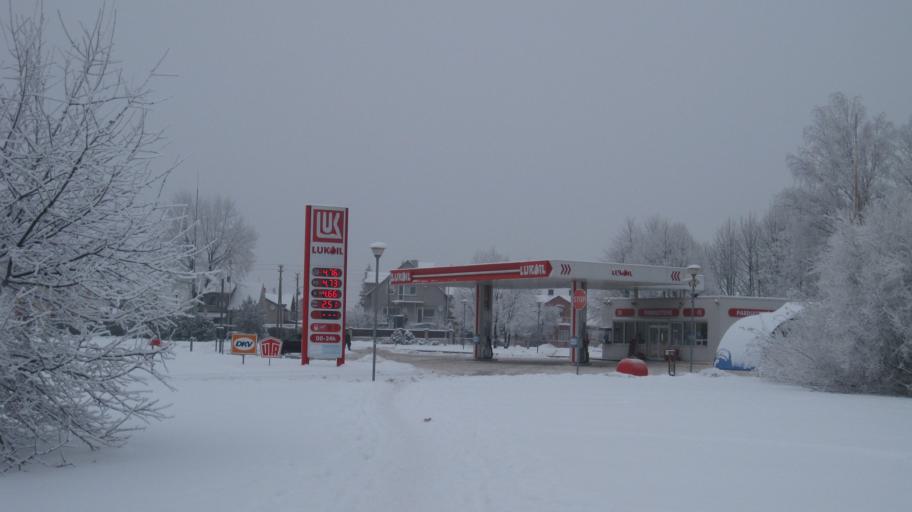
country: LT
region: Kauno apskritis
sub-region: Kaunas
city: Aleksotas
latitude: 54.8658
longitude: 23.8887
